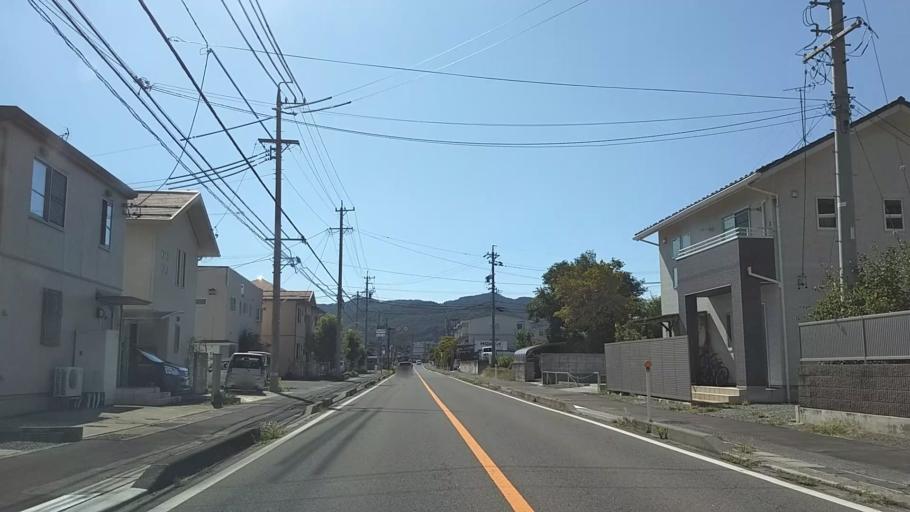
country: JP
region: Nagano
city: Nagano-shi
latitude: 36.6242
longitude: 138.1490
